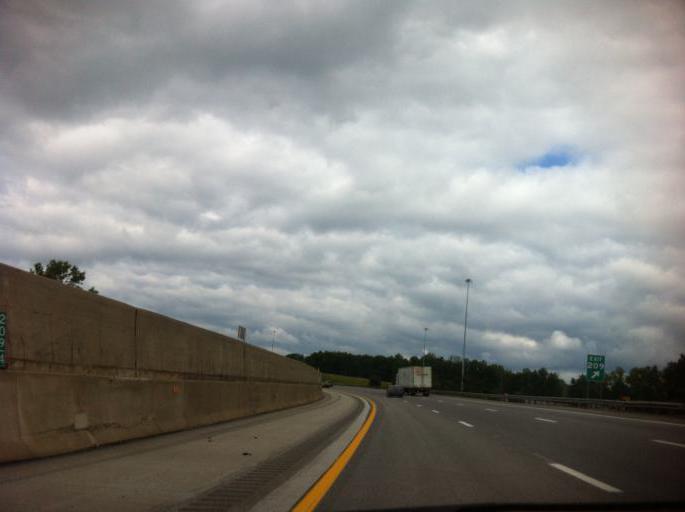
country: US
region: Ohio
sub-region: Trumbull County
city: Newton Falls
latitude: 41.2157
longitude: -80.9512
